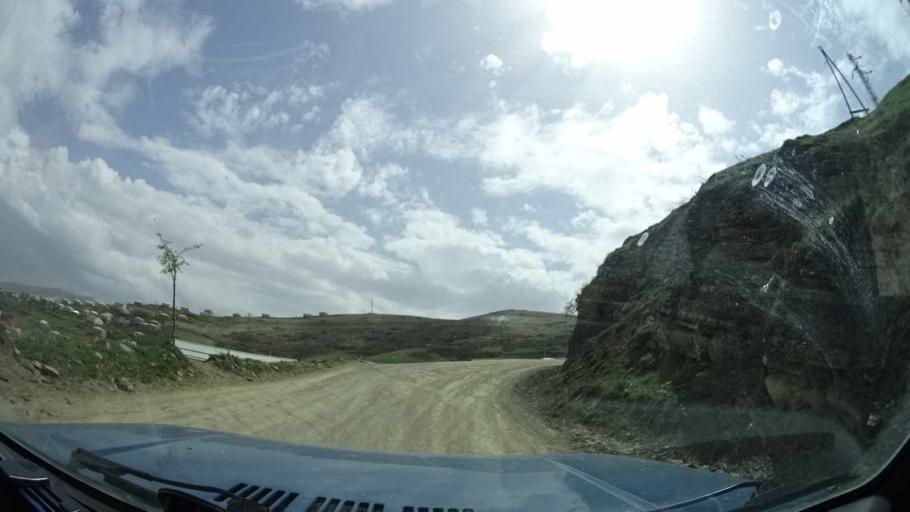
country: RU
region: Dagestan
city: Kubachi
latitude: 42.0926
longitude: 47.5923
